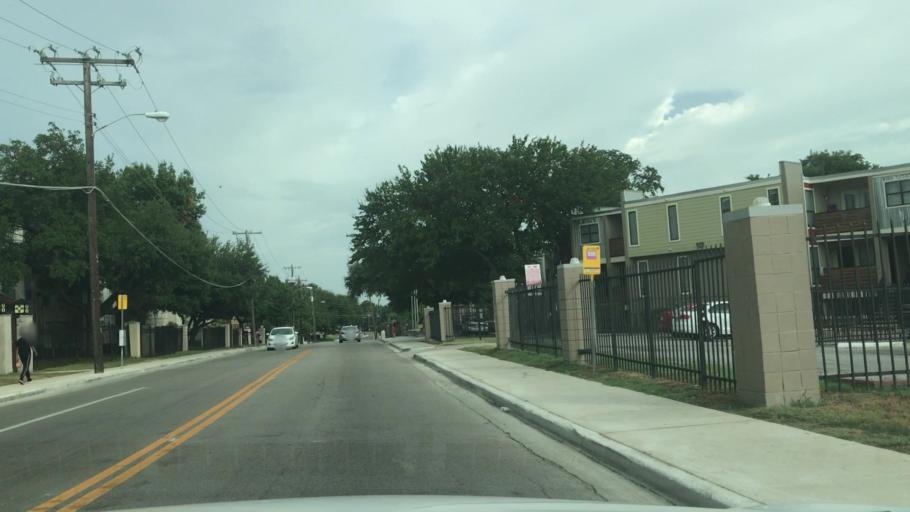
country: US
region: Texas
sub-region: Dallas County
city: University Park
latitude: 32.8699
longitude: -96.7626
